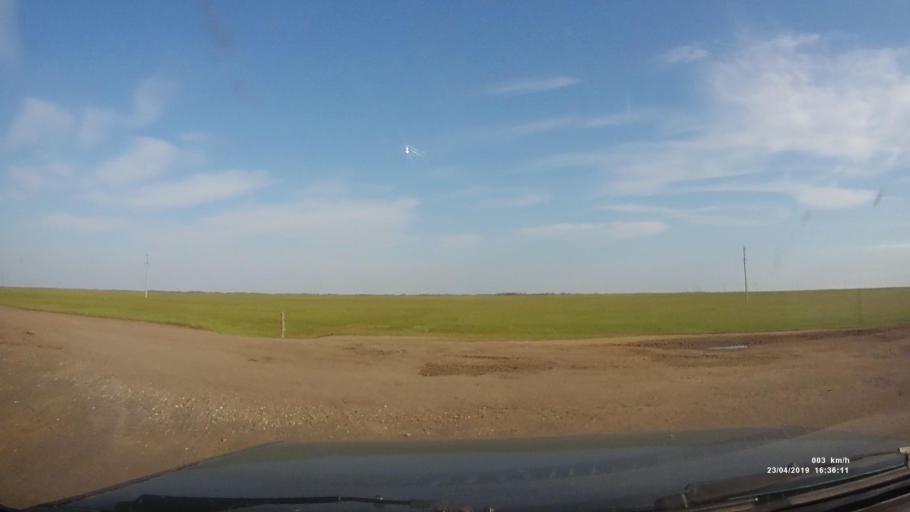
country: RU
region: Kalmykiya
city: Priyutnoye
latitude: 46.3292
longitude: 43.1391
